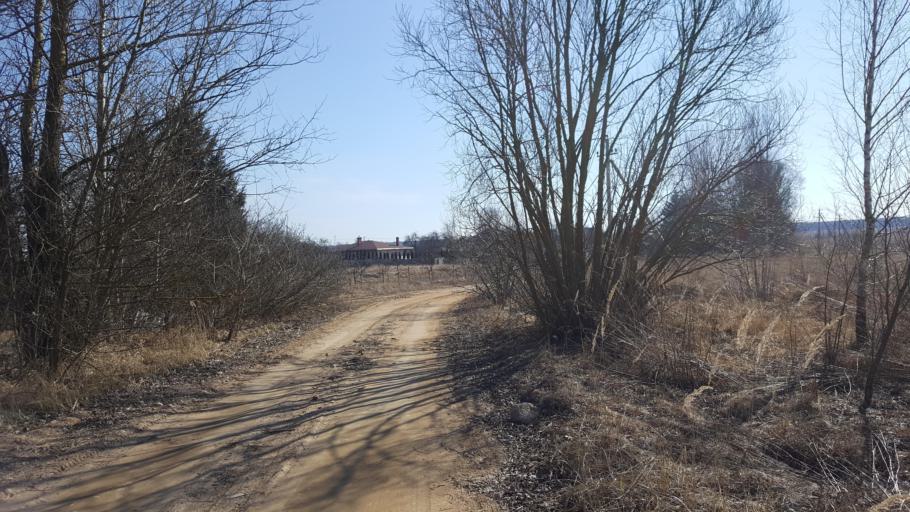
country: BY
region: Brest
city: Kamyanyets
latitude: 52.3642
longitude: 23.7616
